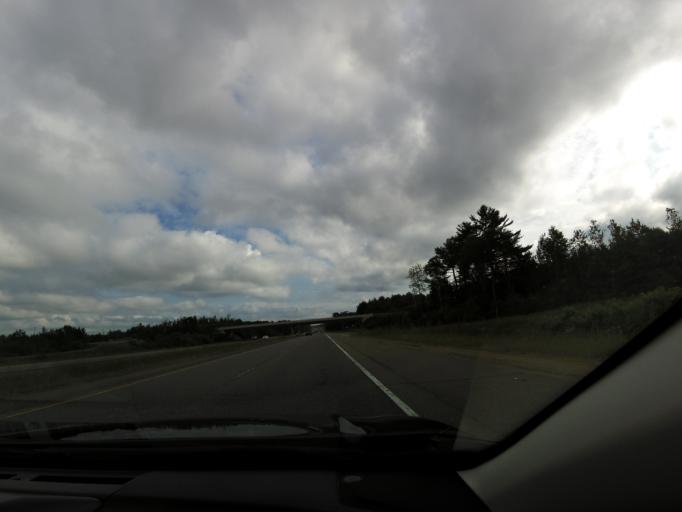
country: CA
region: Ontario
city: Bracebridge
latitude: 44.9938
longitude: -79.3069
